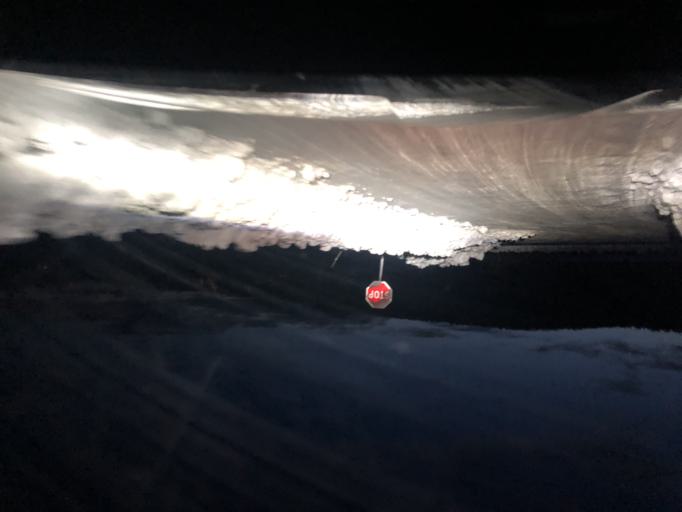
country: SE
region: Vaesternorrland
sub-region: Kramfors Kommun
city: Bollstabruk
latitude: 63.0559
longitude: 17.6323
